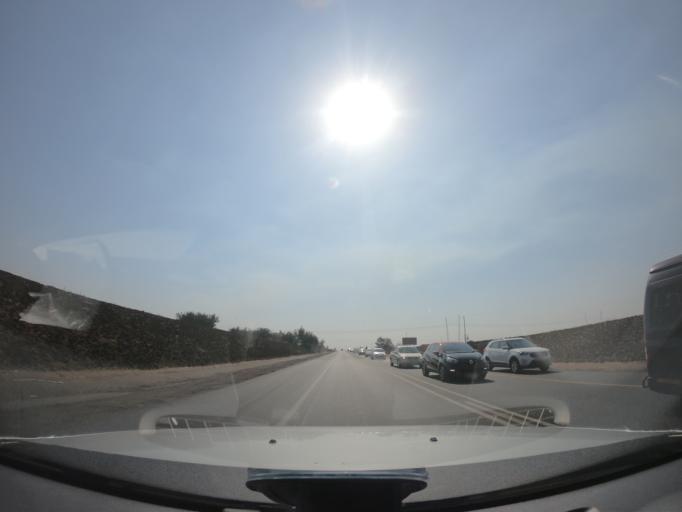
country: ZA
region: Mpumalanga
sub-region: Nkangala District Municipality
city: Middelburg
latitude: -25.8306
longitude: 29.4600
